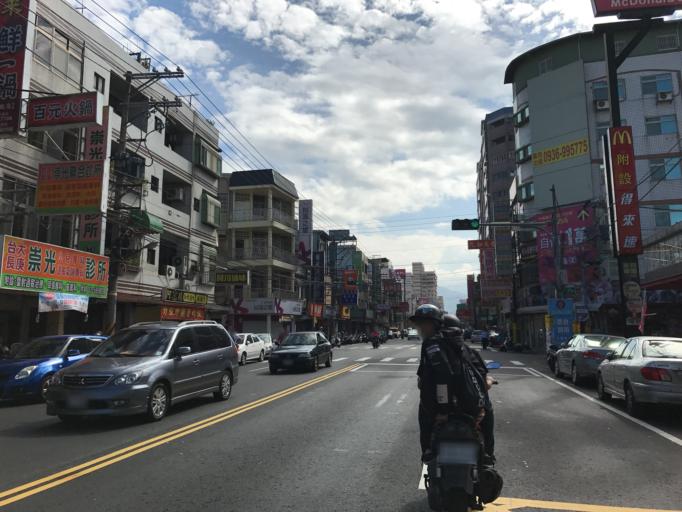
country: TW
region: Taiwan
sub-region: Hsinchu
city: Zhubei
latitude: 24.7440
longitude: 121.0832
